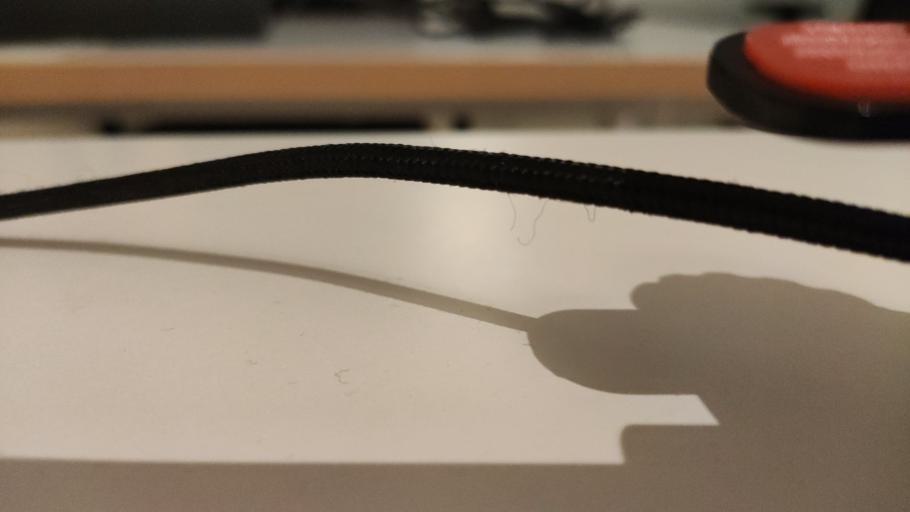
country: RU
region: Moskovskaya
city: Novoye
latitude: 55.6276
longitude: 38.9443
